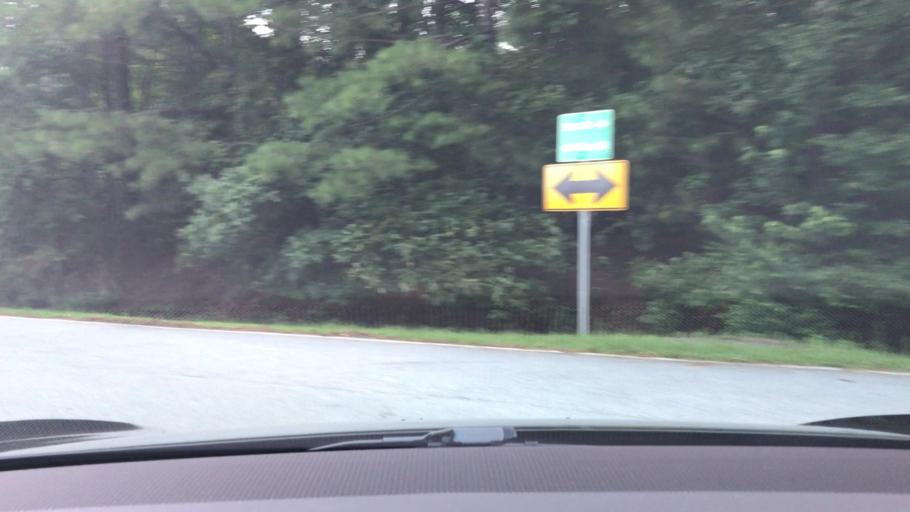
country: US
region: Georgia
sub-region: Gwinnett County
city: Suwanee
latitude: 34.0741
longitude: -84.0865
